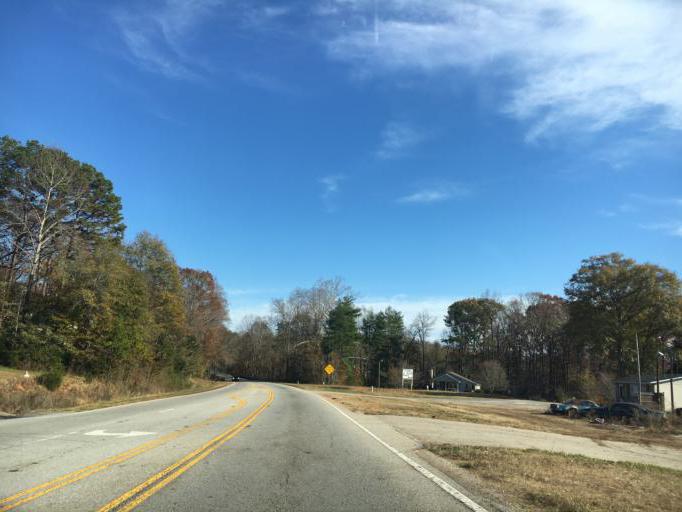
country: US
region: South Carolina
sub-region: Spartanburg County
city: Wellford
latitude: 34.9599
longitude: -82.0791
